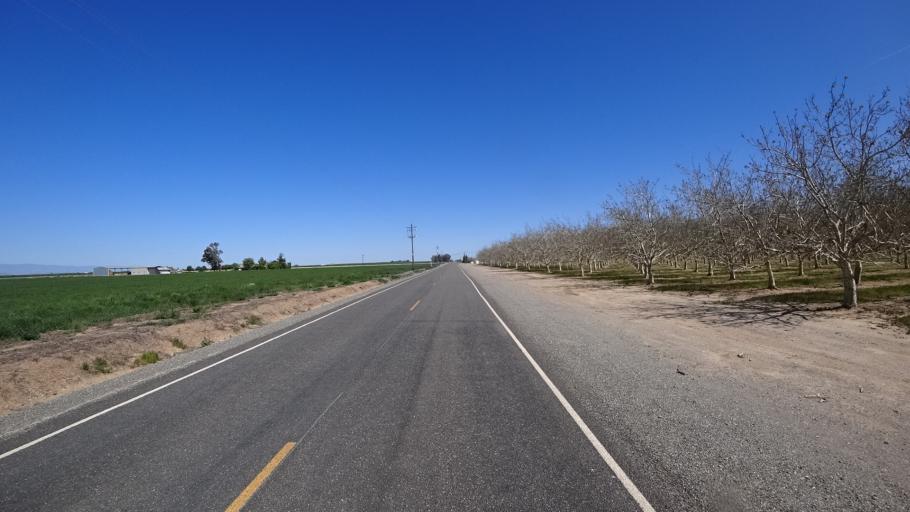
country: US
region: California
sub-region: Glenn County
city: Hamilton City
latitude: 39.6491
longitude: -122.1037
